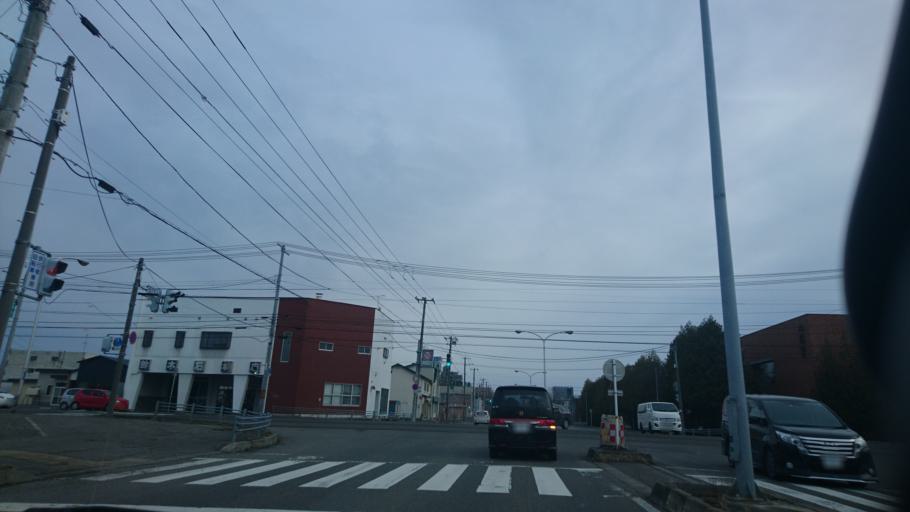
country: JP
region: Hokkaido
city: Obihiro
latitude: 42.9321
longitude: 143.1992
